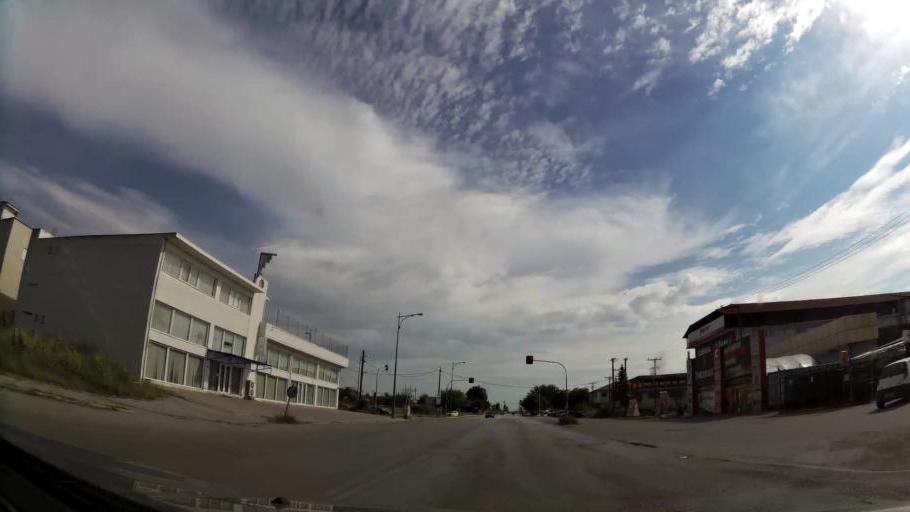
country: GR
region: Central Macedonia
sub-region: Nomos Pierias
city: Katerini
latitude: 40.2840
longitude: 22.5195
